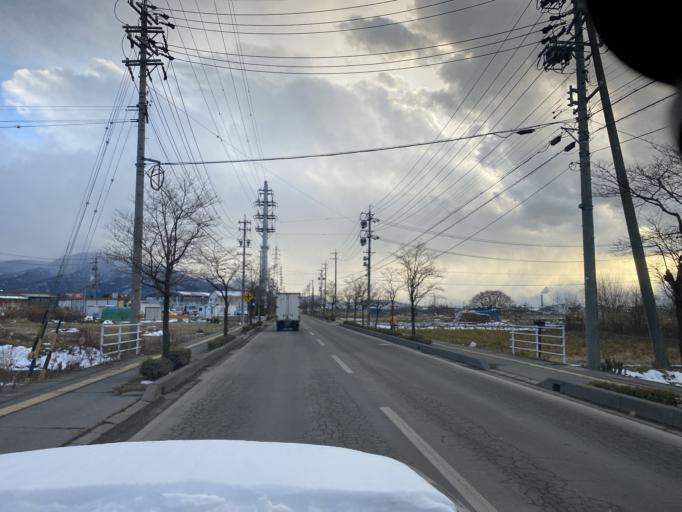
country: JP
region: Nagano
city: Nagano-shi
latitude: 36.6384
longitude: 138.2419
